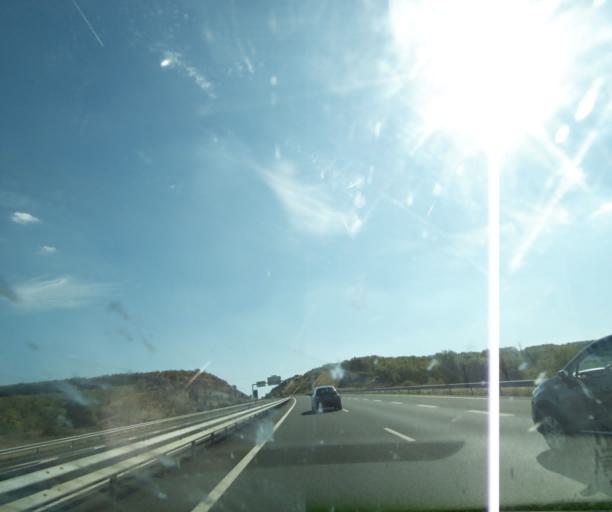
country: FR
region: Limousin
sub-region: Departement de la Correze
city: Brive-la-Gaillarde
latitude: 45.0611
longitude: 1.5064
